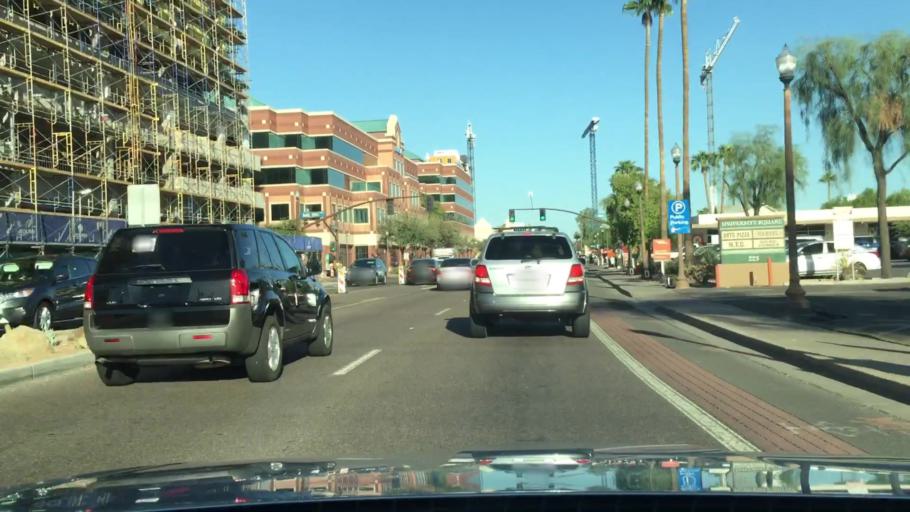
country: US
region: Arizona
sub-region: Maricopa County
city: Tempe Junction
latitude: 33.4219
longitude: -111.9433
